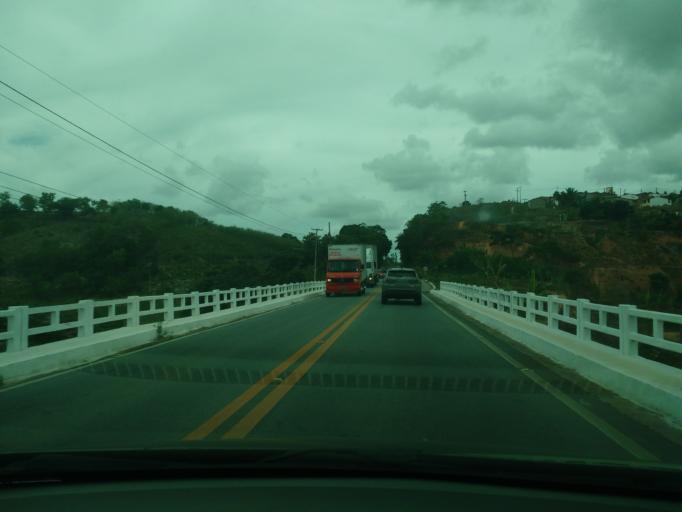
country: BR
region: Alagoas
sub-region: Uniao Dos Palmares
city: Uniao dos Palmares
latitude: -9.2421
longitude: -36.0114
